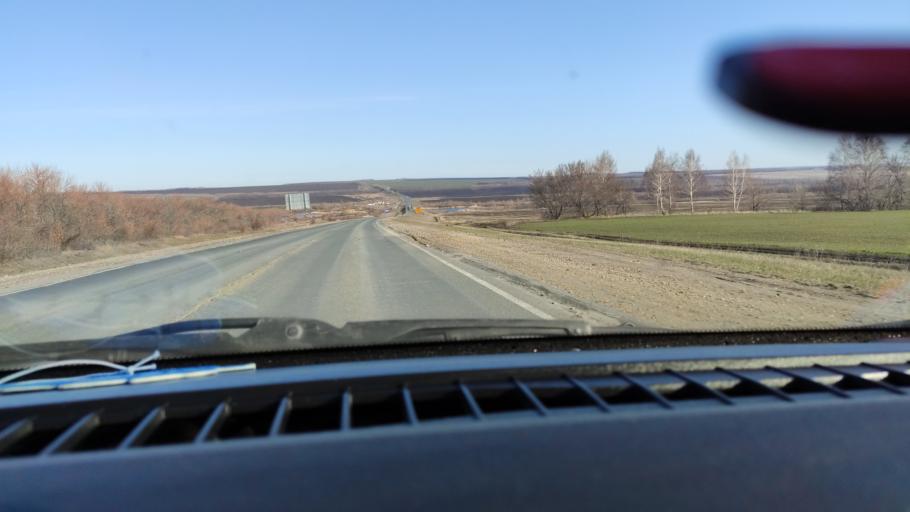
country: RU
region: Saratov
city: Dukhovnitskoye
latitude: 52.7270
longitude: 48.2601
